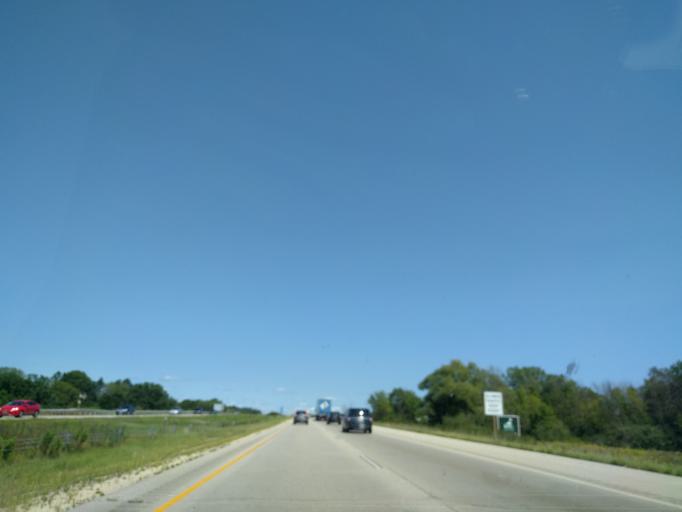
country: US
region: Wisconsin
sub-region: Ozaukee County
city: Grafton
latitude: 43.2921
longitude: -87.9205
